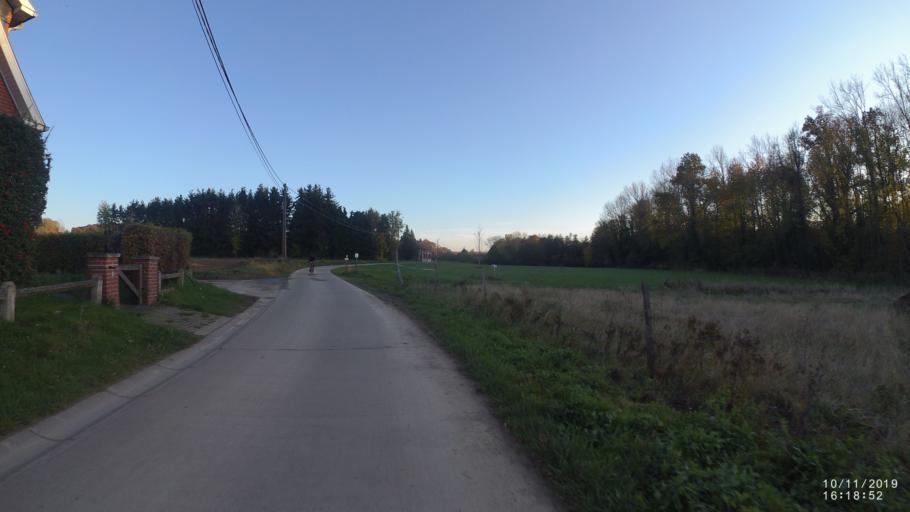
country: BE
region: Flanders
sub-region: Provincie Vlaams-Brabant
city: Lubbeek
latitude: 50.8872
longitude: 4.8489
